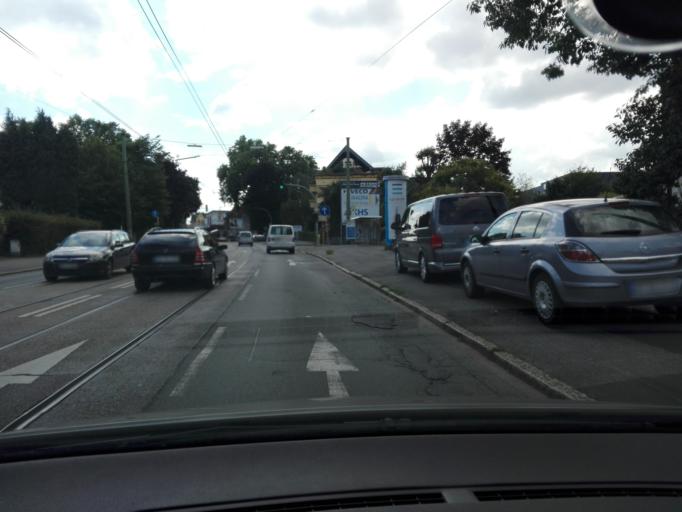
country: DE
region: North Rhine-Westphalia
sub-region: Regierungsbezirk Arnsberg
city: Dortmund
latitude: 51.5199
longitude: 7.5145
